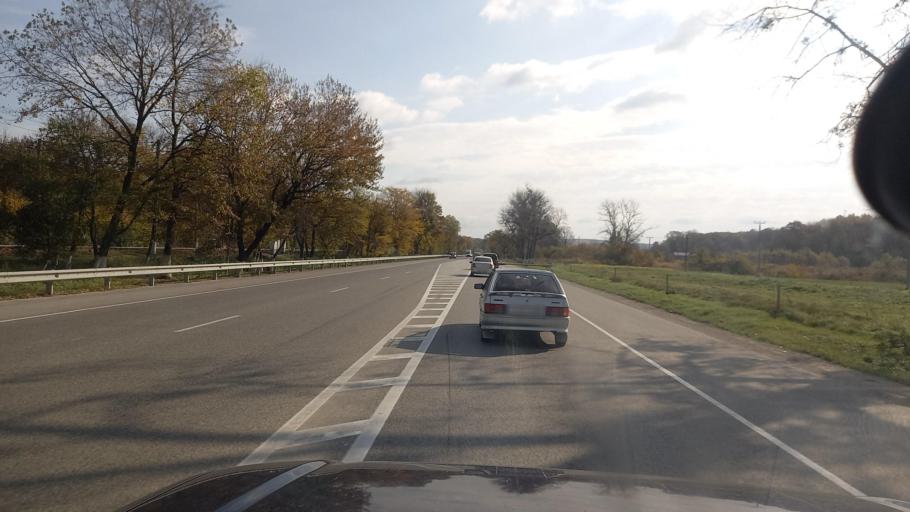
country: RU
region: Krasnodarskiy
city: Gayduk
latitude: 44.8724
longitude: 37.8327
